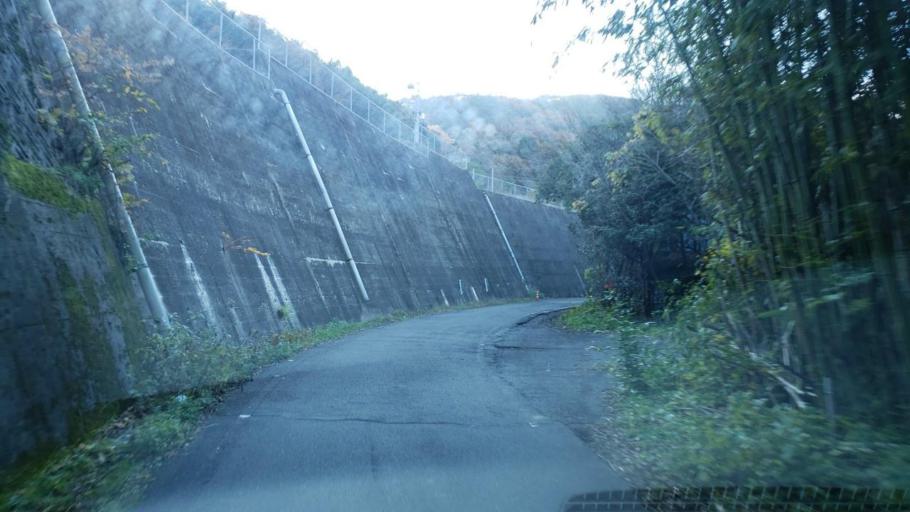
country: JP
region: Tokushima
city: Wakimachi
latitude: 34.0753
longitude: 134.0815
